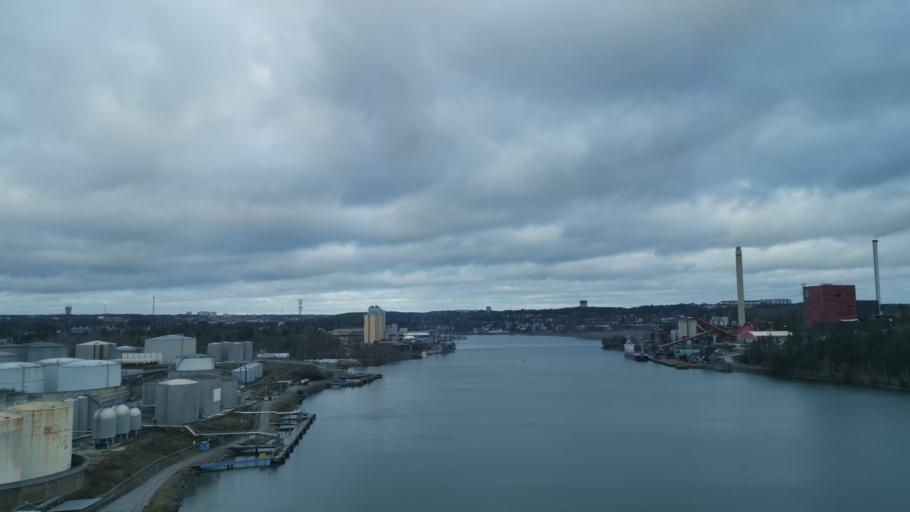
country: SE
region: Stockholm
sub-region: Sodertalje Kommun
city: Pershagen
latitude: 59.1673
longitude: 17.6655
